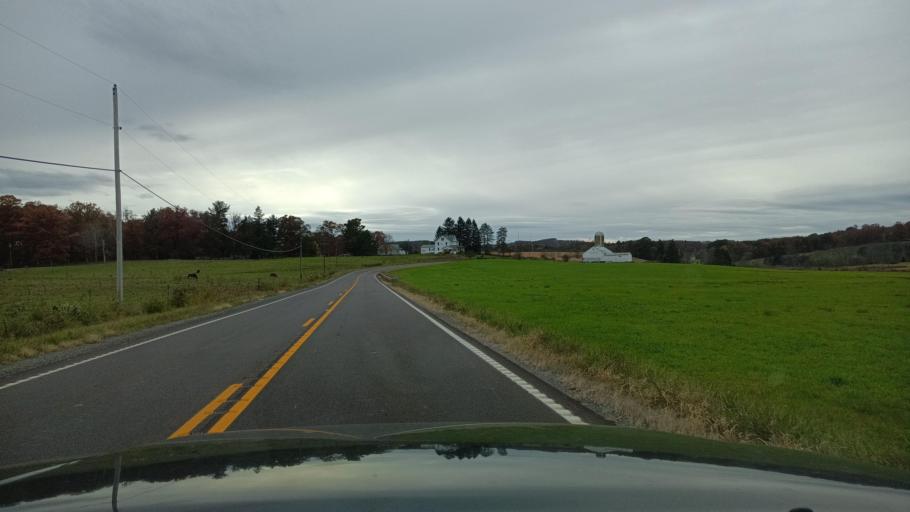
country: US
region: Maryland
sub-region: Garrett County
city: Oakland
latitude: 39.3088
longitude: -79.4651
